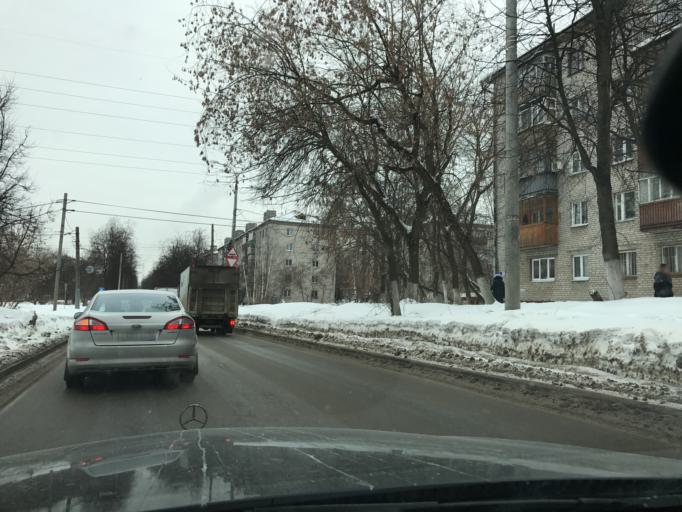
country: RU
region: Nizjnij Novgorod
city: Gorbatovka
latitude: 56.2472
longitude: 43.8389
